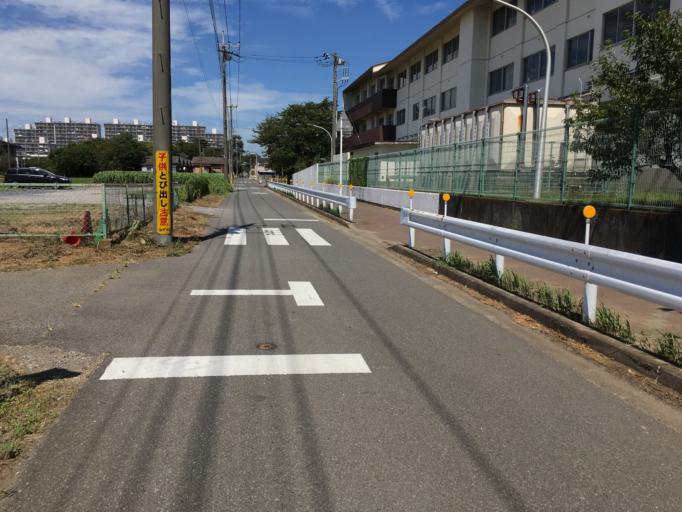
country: JP
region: Chiba
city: Nagareyama
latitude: 35.8250
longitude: 139.9024
